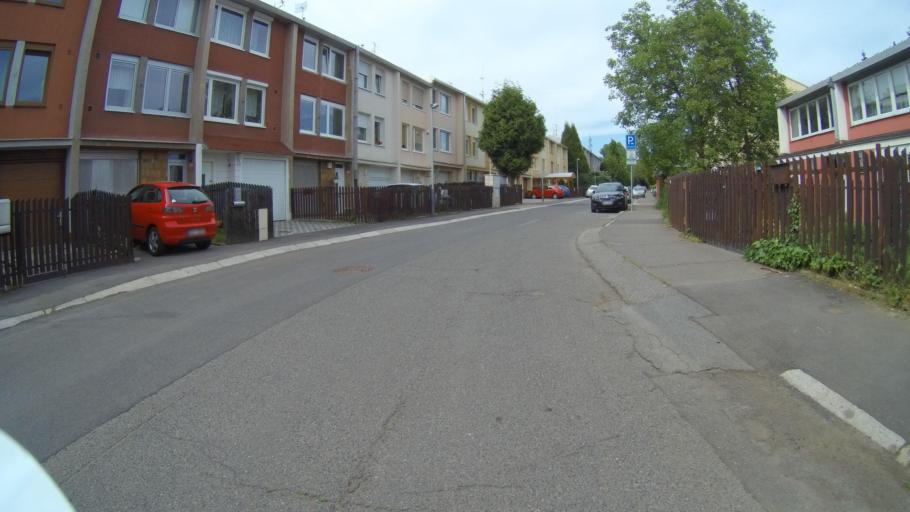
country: CZ
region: Praha
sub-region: Praha 9
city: Strizkov
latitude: 50.1378
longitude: 14.4762
